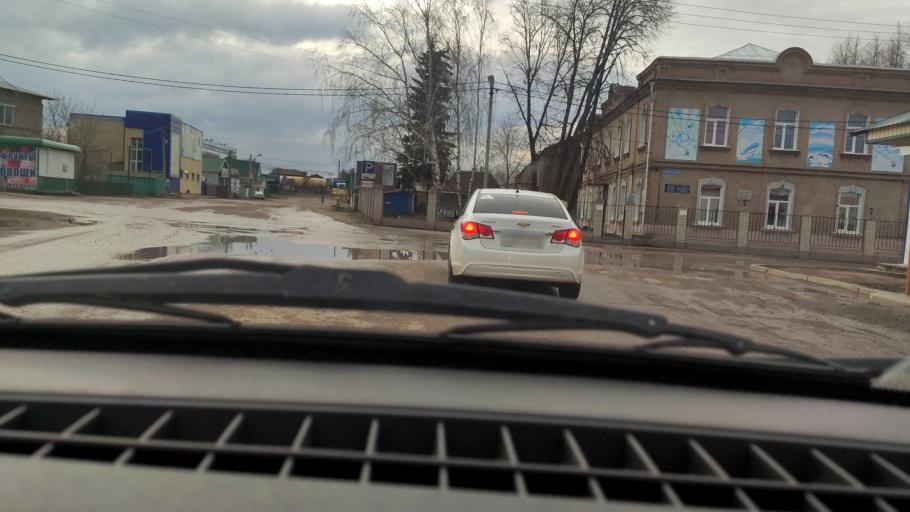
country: RU
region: Bashkortostan
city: Davlekanovo
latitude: 54.2113
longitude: 55.0263
